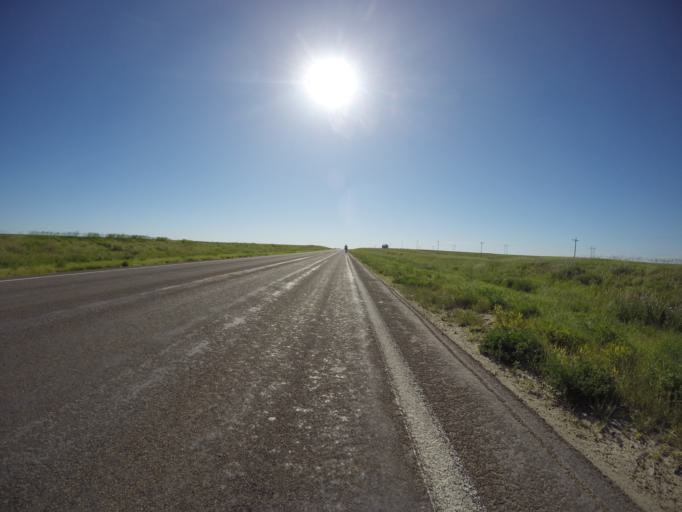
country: US
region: Kansas
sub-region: Norton County
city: Norton
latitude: 39.8281
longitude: -100.0382
